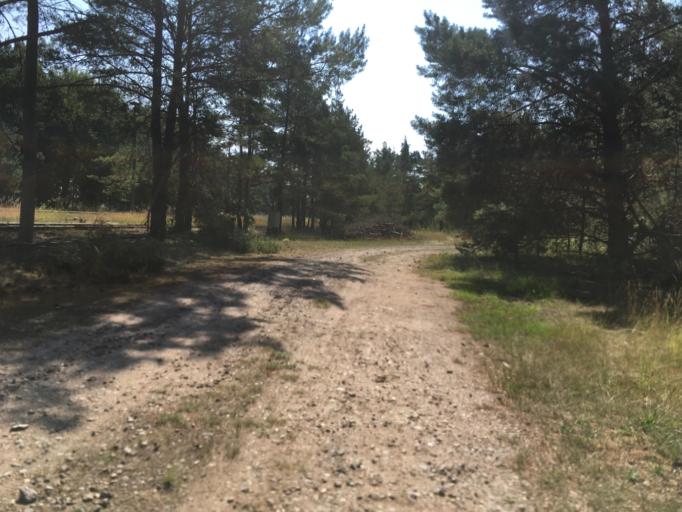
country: DE
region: Brandenburg
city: Milmersdorf
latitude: 53.0958
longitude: 13.6445
